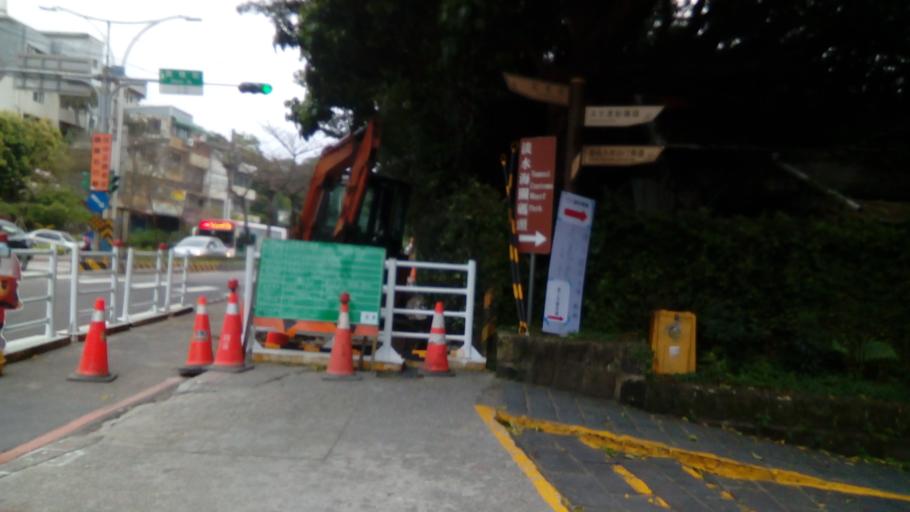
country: TW
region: Taipei
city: Taipei
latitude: 25.1744
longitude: 121.4333
